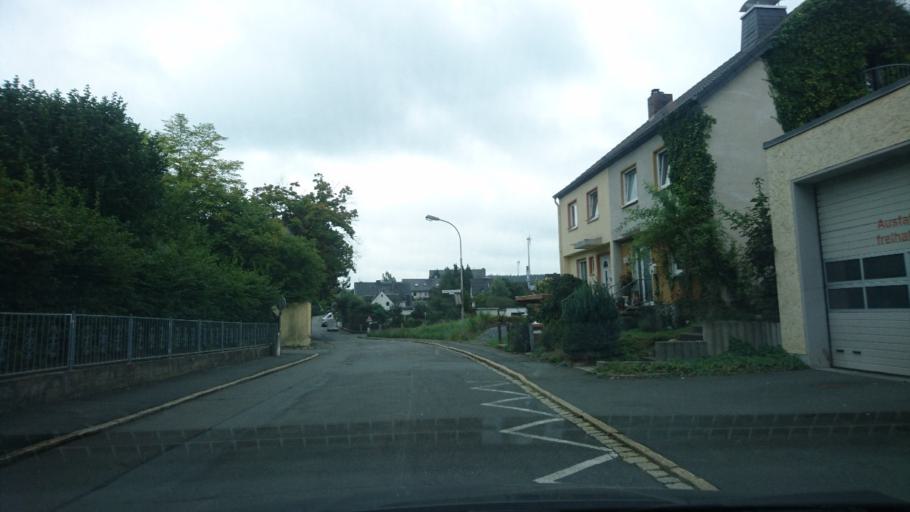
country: DE
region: Bavaria
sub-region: Upper Franconia
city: Naila
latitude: 50.3254
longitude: 11.7119
